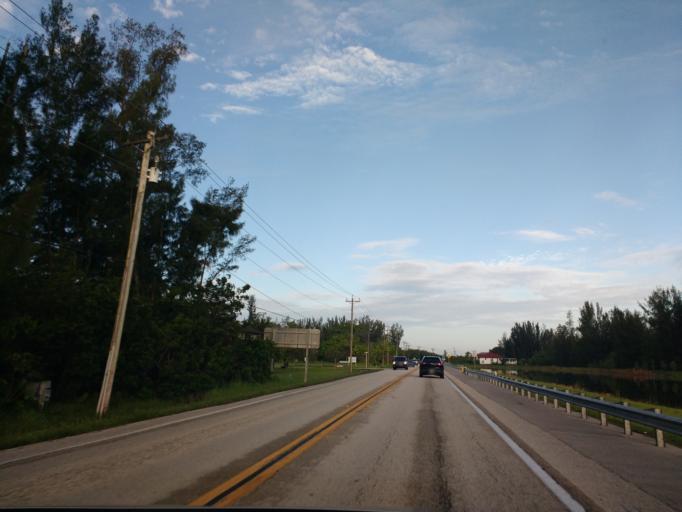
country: US
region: Florida
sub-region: Lee County
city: Pine Island Center
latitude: 26.6376
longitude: -82.0442
